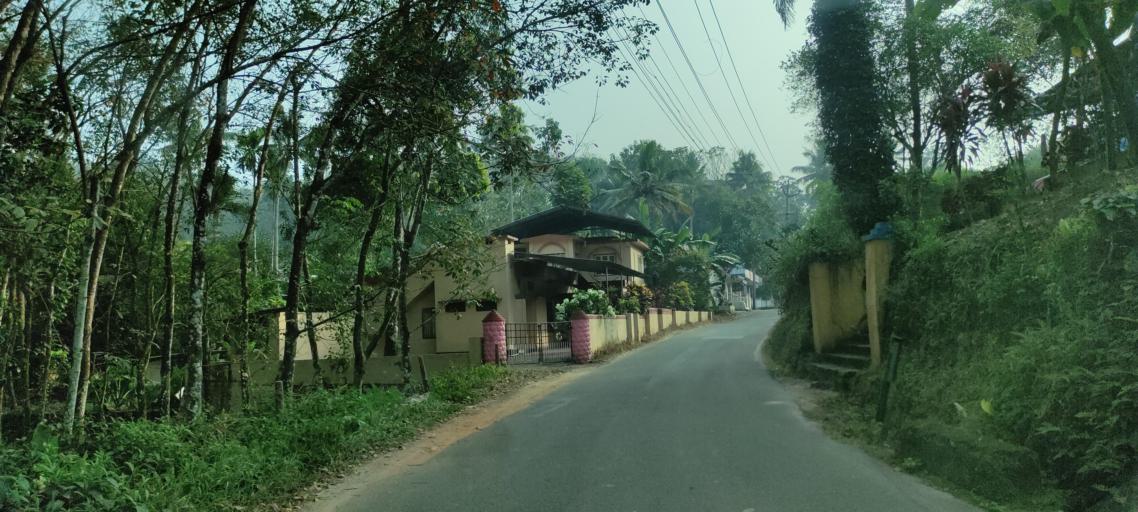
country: IN
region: Kerala
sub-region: Ernakulam
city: Piravam
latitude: 9.7840
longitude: 76.4990
